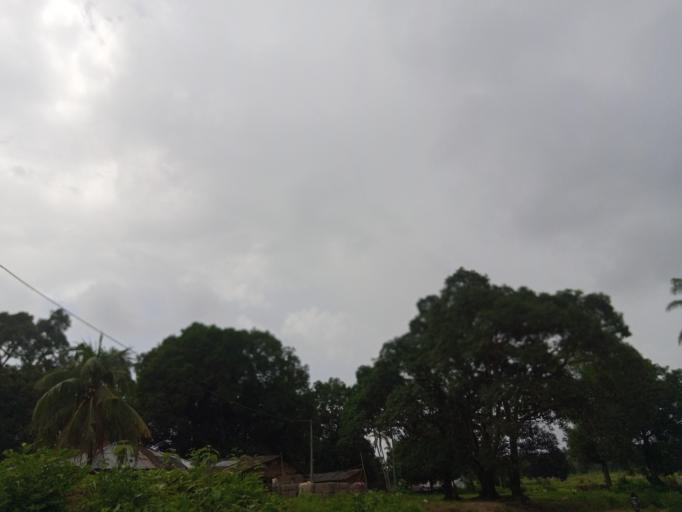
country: SL
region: Northern Province
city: Sawkta
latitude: 8.6335
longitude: -13.2018
